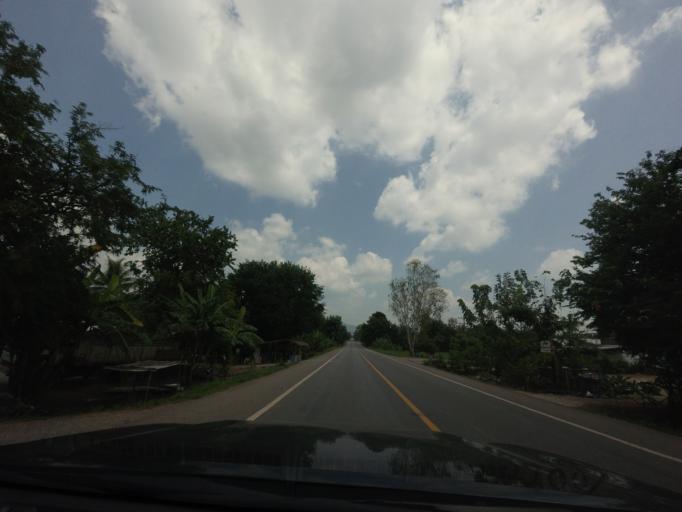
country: TH
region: Phitsanulok
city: Chat Trakan
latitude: 17.3056
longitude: 100.4651
